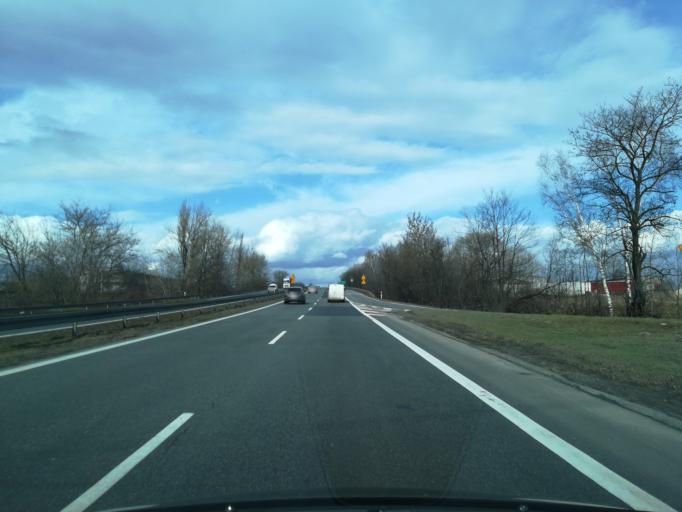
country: PL
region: Silesian Voivodeship
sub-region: Dabrowa Gornicza
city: Dabrowa Gornicza
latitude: 50.3280
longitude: 19.2425
